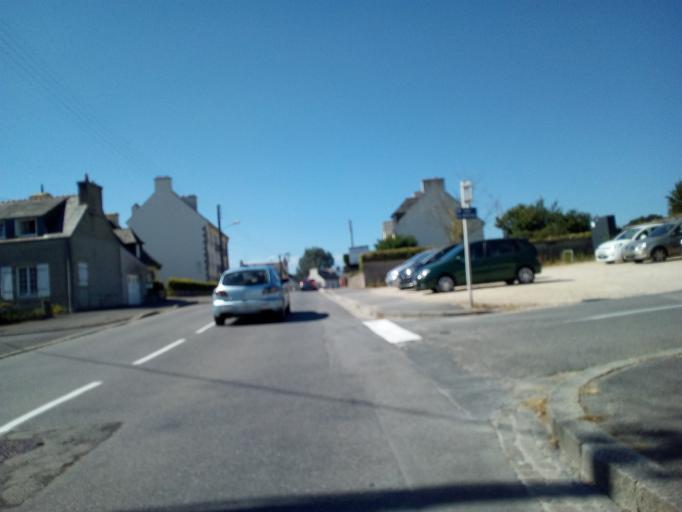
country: FR
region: Brittany
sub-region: Departement du Finistere
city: Landivisiau
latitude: 48.5137
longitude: -4.0714
